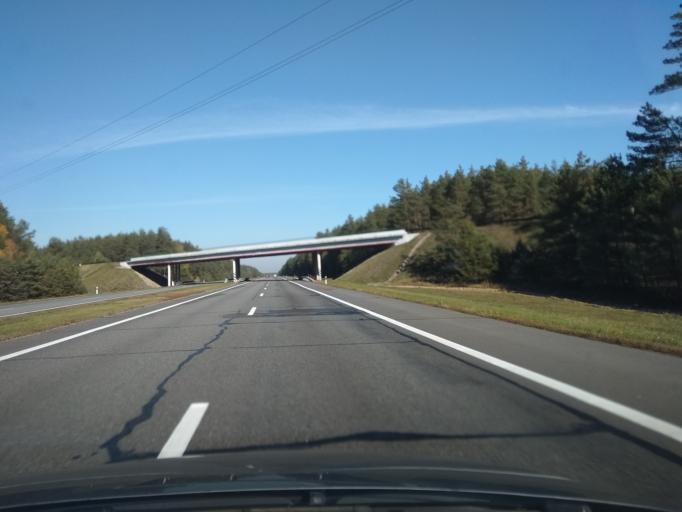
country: BY
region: Brest
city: Baranovichi
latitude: 52.9978
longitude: 25.7630
